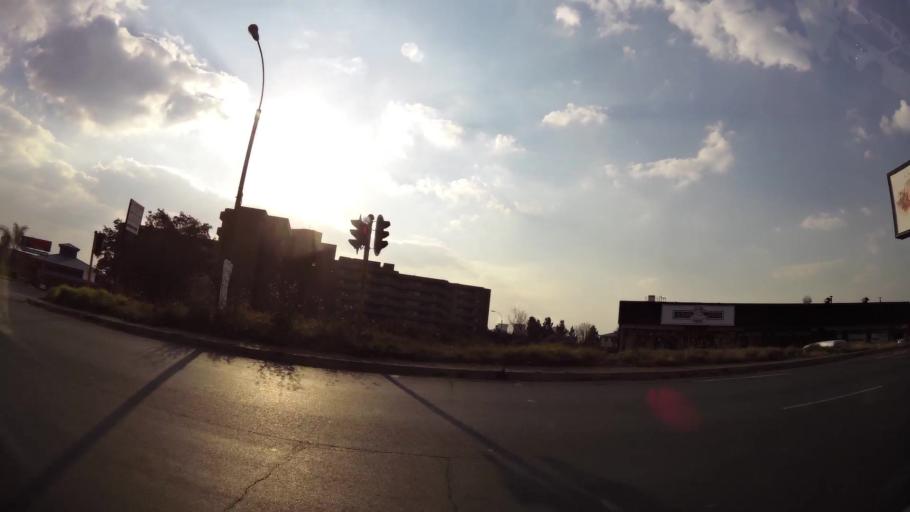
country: ZA
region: Gauteng
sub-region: City of Johannesburg Metropolitan Municipality
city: Modderfontein
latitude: -26.1321
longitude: 28.1998
